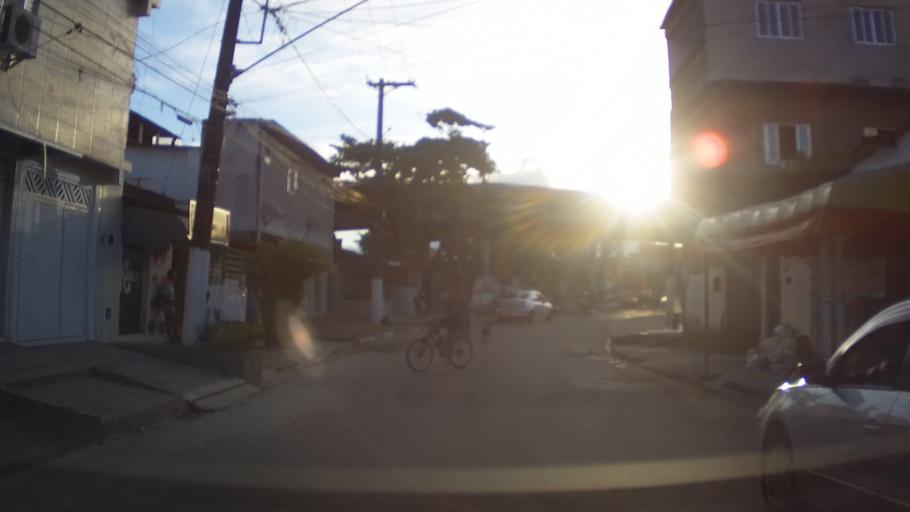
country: BR
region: Sao Paulo
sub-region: Sao Vicente
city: Sao Vicente
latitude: -23.9697
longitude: -46.4000
